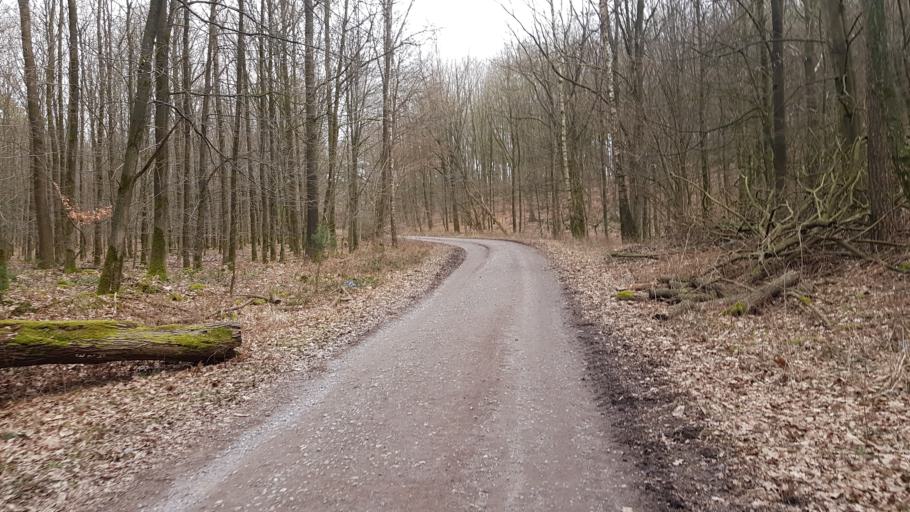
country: DE
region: North Rhine-Westphalia
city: Oer-Erkenschwick
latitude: 51.6753
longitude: 7.2532
